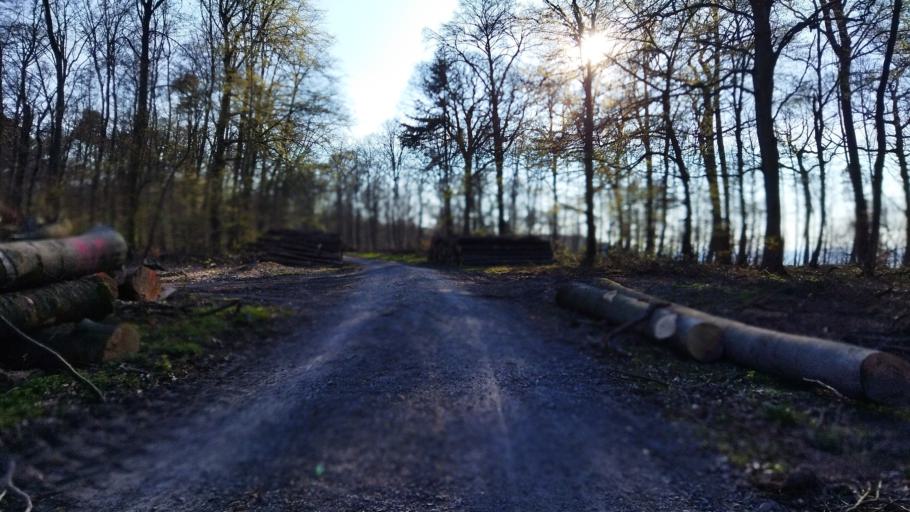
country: DE
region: Baden-Wuerttemberg
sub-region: Karlsruhe Region
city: Sternenfels
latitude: 49.0500
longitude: 8.8718
